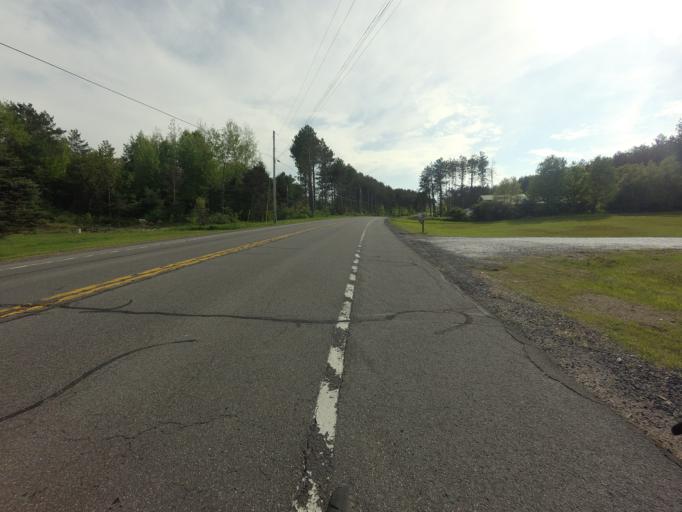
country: US
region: New York
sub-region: St. Lawrence County
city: Gouverneur
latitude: 44.1663
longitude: -75.3041
